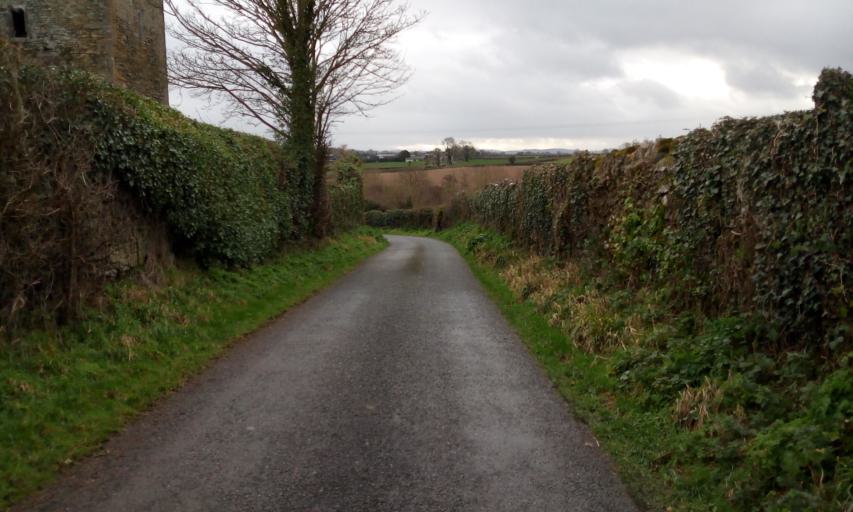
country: IE
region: Leinster
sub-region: Kilkenny
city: Callan
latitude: 52.5440
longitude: -7.3159
